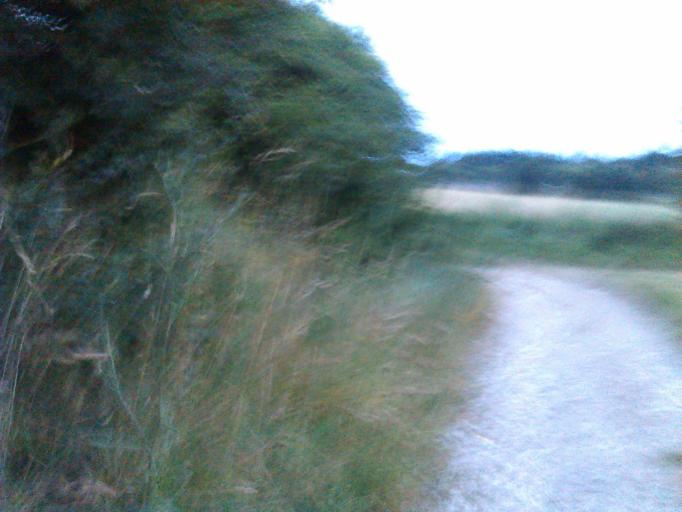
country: IT
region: Tuscany
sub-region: Province of Arezzo
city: Viciomaggio
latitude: 43.4440
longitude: 11.7730
